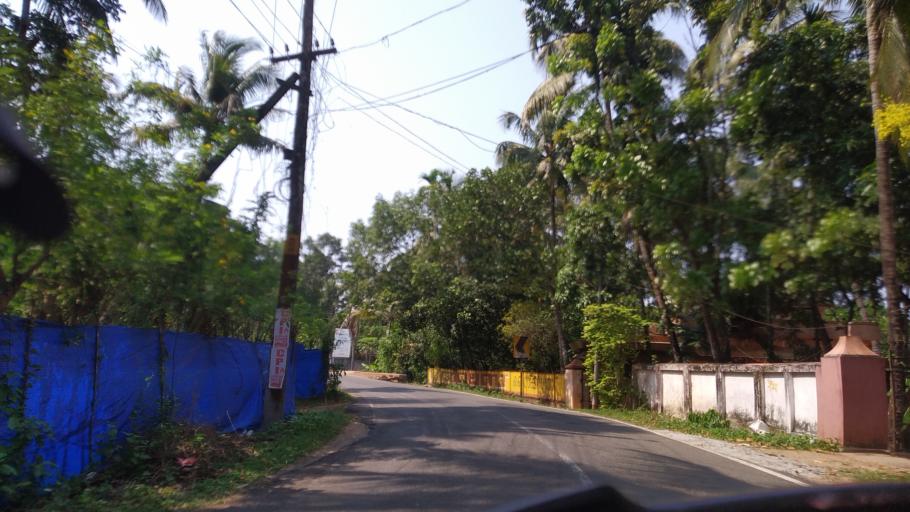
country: IN
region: Kerala
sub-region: Thrissur District
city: Irinjalakuda
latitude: 10.2981
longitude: 76.1326
